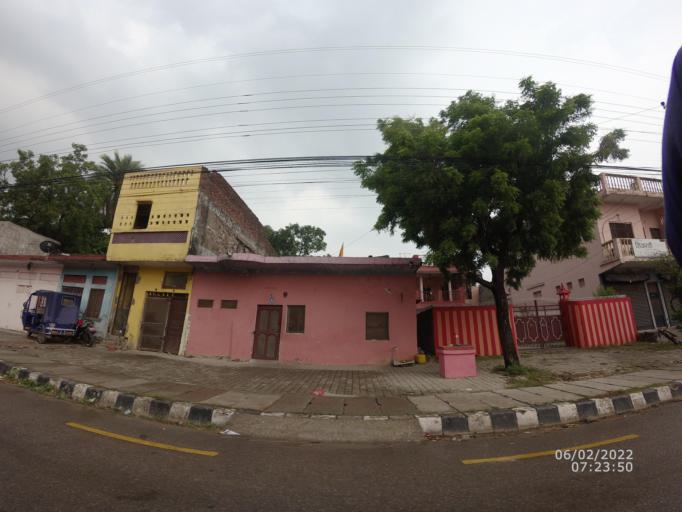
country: NP
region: Western Region
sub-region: Lumbini Zone
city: Bhairahawa
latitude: 27.4964
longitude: 83.4470
